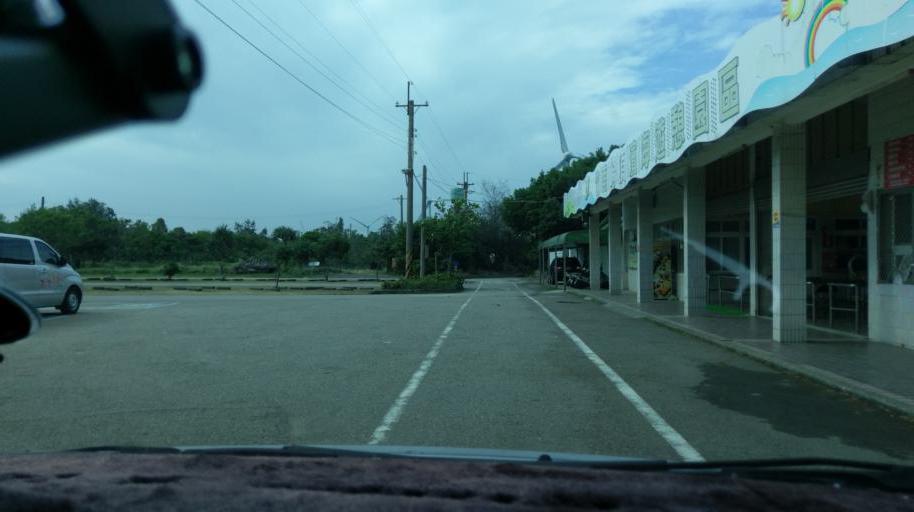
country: TW
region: Taiwan
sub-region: Hsinchu
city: Hsinchu
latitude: 24.7225
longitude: 120.8675
